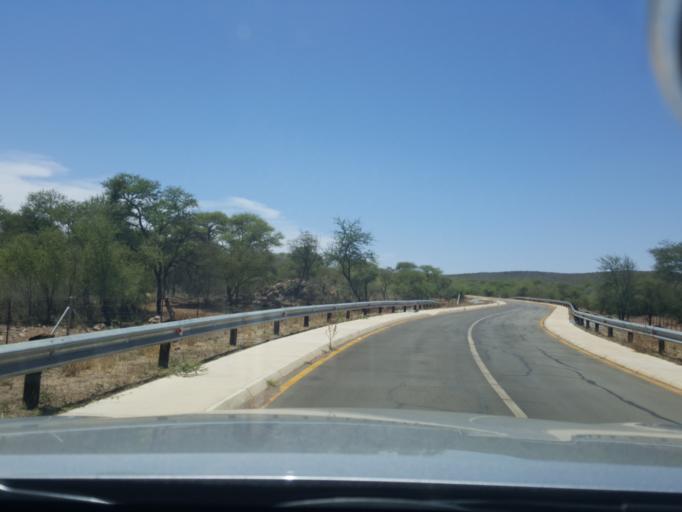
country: BW
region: South East
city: Ramotswa
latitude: -24.8723
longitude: 25.8832
